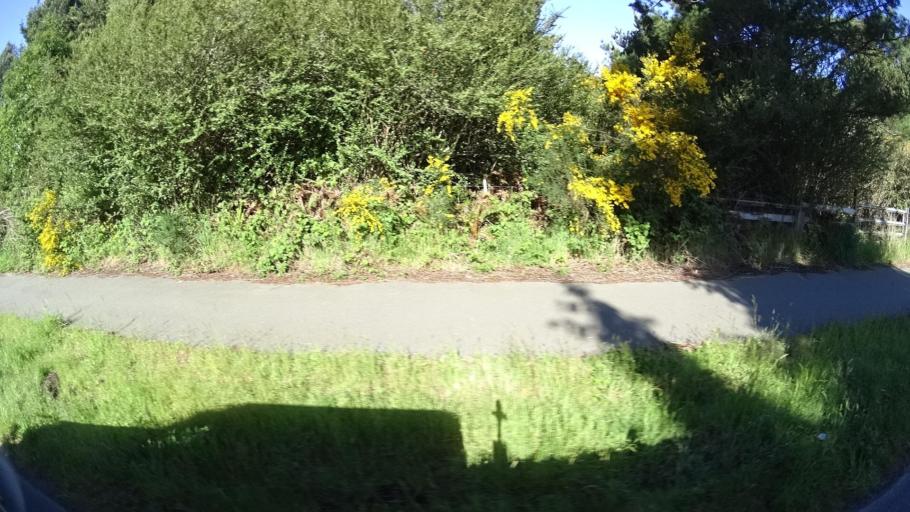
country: US
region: California
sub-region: Humboldt County
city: McKinleyville
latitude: 40.9747
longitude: -124.0959
